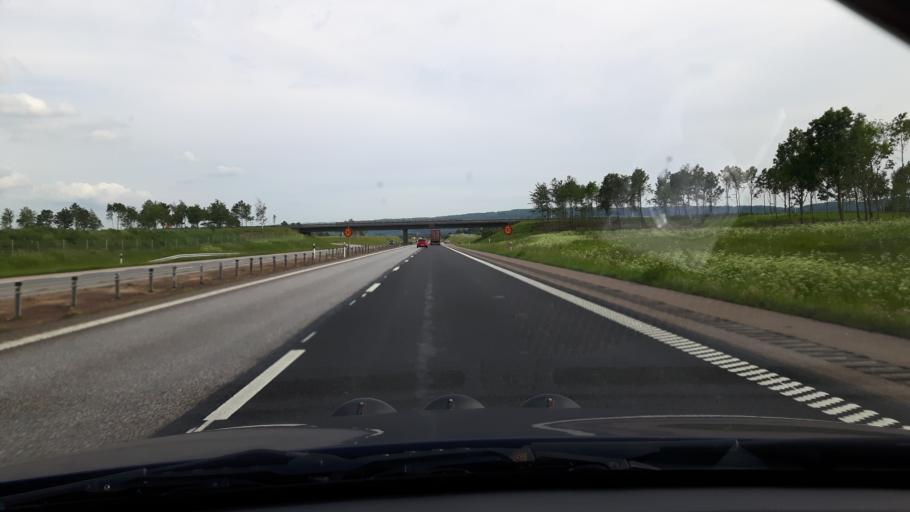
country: SE
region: Halland
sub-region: Laholms Kommun
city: Mellbystrand
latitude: 56.4549
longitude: 12.9463
